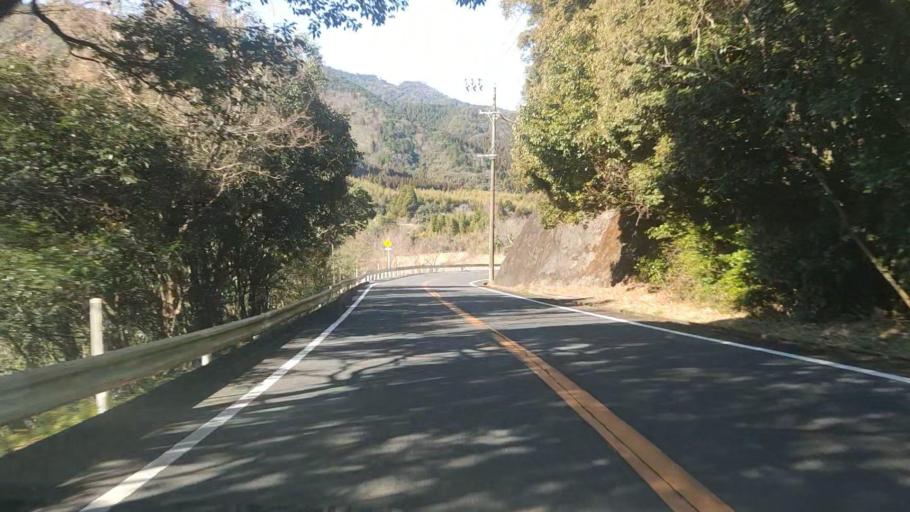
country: JP
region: Oita
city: Saiki
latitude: 32.8974
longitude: 131.9373
